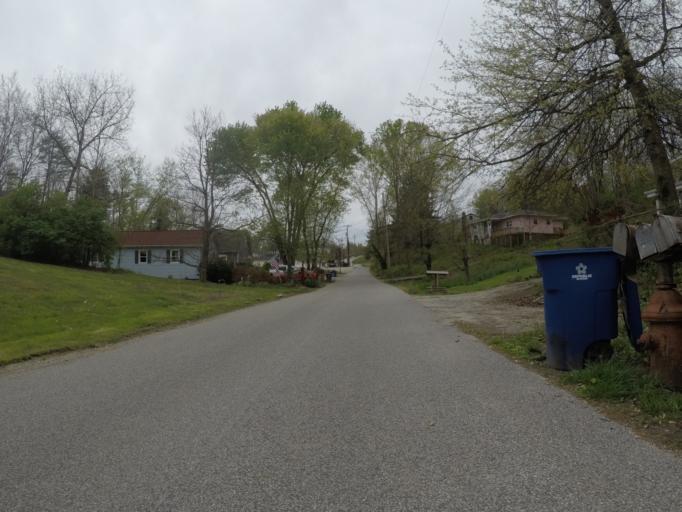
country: US
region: West Virginia
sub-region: Cabell County
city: Pea Ridge
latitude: 38.4135
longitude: -82.3365
